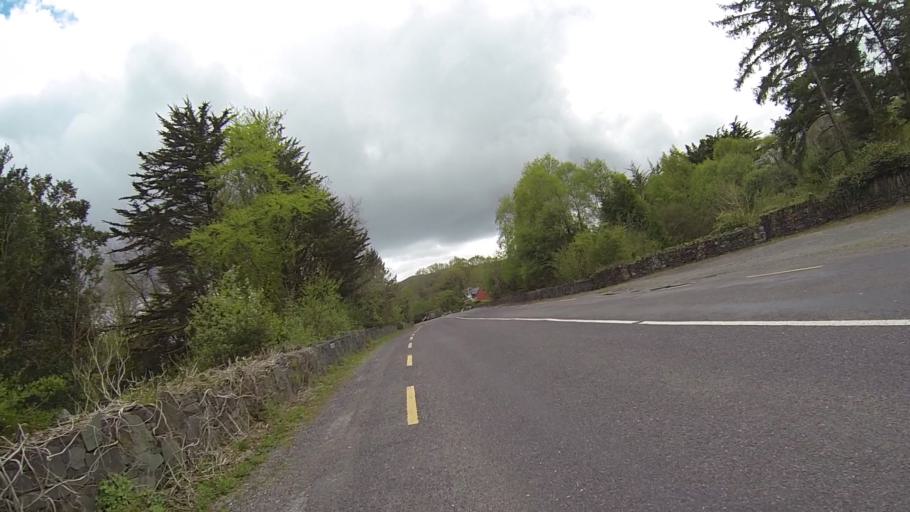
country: IE
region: Munster
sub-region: County Cork
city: Bantry
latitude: 51.7358
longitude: -9.5589
